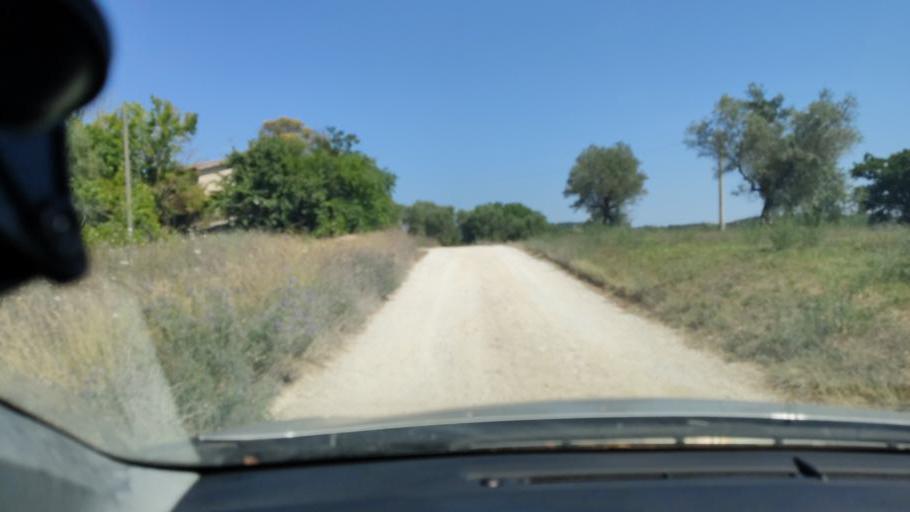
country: IT
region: Umbria
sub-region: Provincia di Terni
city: Fornole
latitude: 42.5448
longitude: 12.4409
